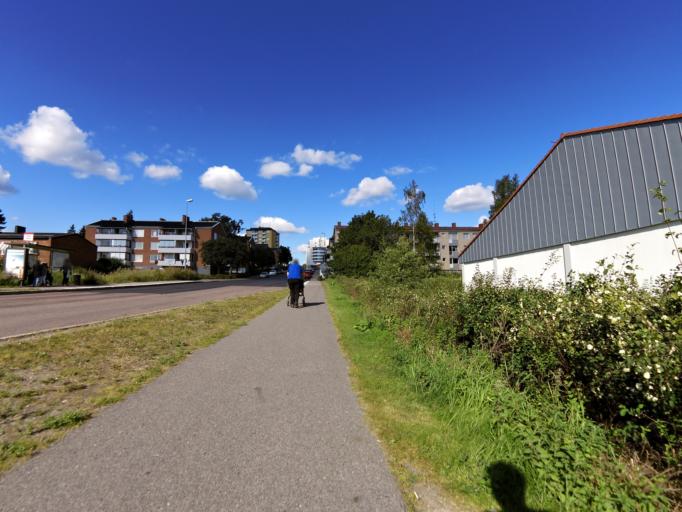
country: SE
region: Gaevleborg
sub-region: Gavle Kommun
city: Gavle
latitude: 60.6936
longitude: 17.1490
